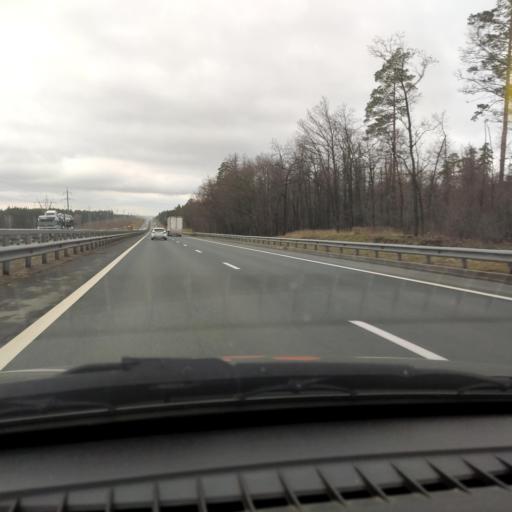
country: RU
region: Samara
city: Povolzhskiy
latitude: 53.5178
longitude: 49.7791
